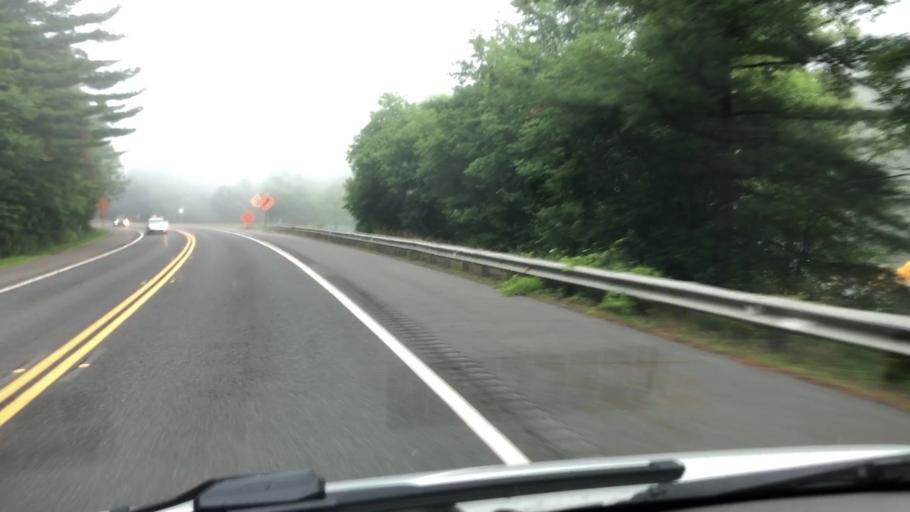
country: US
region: Massachusetts
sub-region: Berkshire County
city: Hinsdale
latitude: 42.4909
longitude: -72.9708
